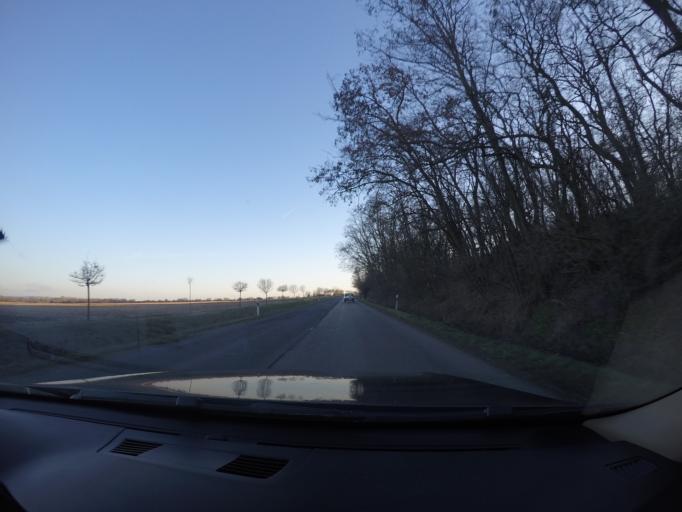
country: HU
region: Pest
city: Dunabogdany
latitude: 47.7749
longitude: 19.0562
